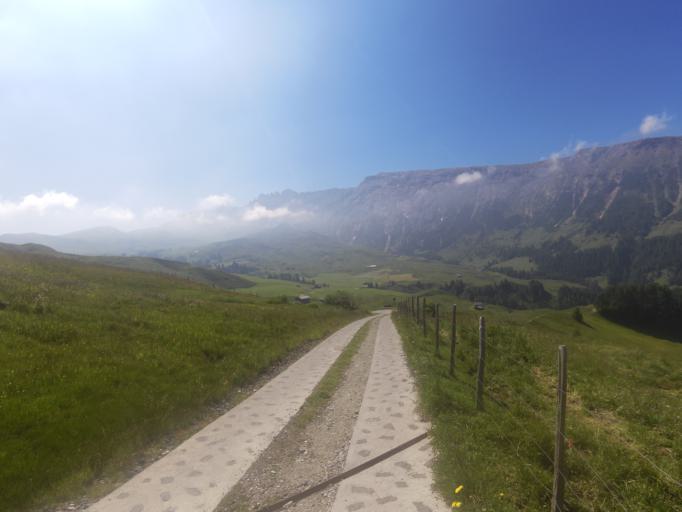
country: IT
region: Trentino-Alto Adige
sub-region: Bolzano
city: Siusi
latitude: 46.5251
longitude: 11.6062
